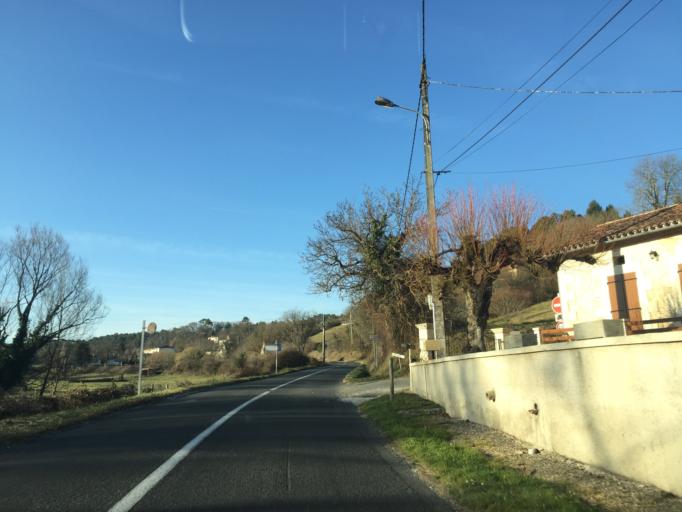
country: FR
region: Aquitaine
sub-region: Departement de la Dordogne
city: Neuvic
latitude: 45.1399
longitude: 0.4480
